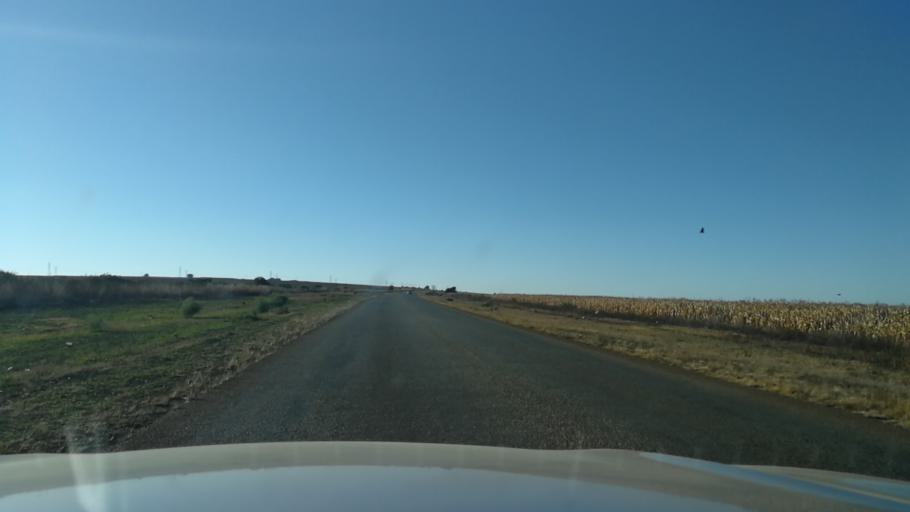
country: ZA
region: North-West
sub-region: Bojanala Platinum District Municipality
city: Rustenburg
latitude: -25.9851
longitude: 27.2735
